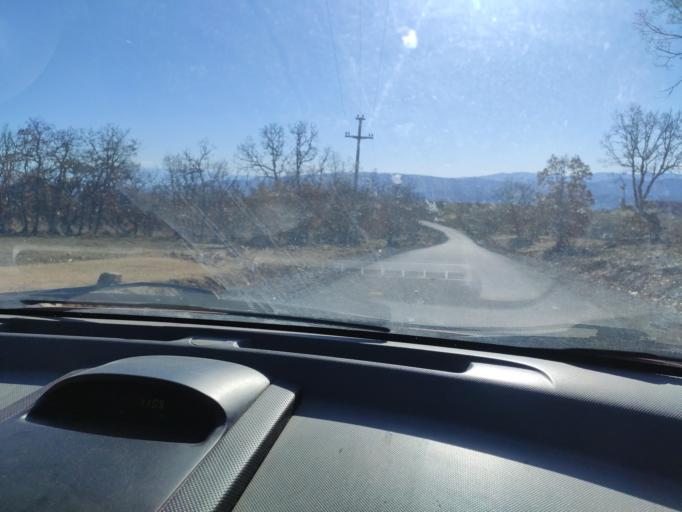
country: MK
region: Radovis
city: Radovish
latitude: 41.6652
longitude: 22.4083
